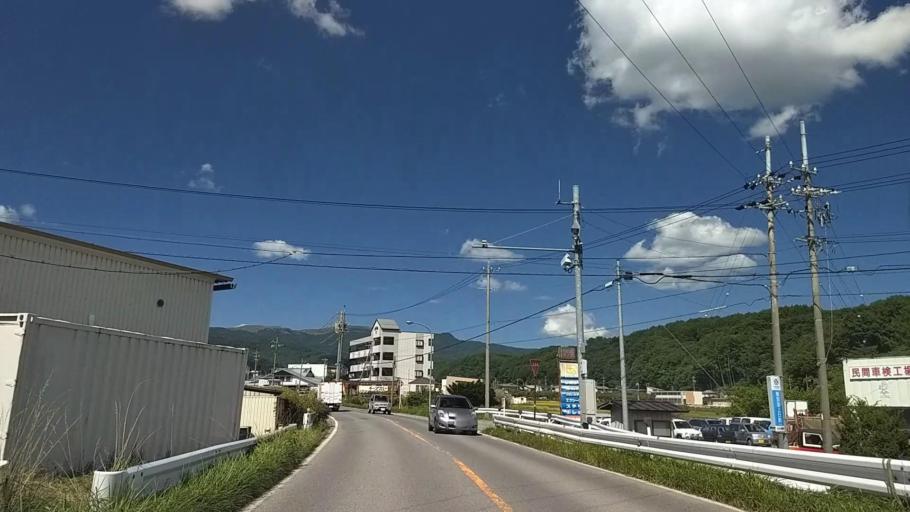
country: JP
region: Nagano
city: Chino
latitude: 36.0058
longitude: 138.1751
